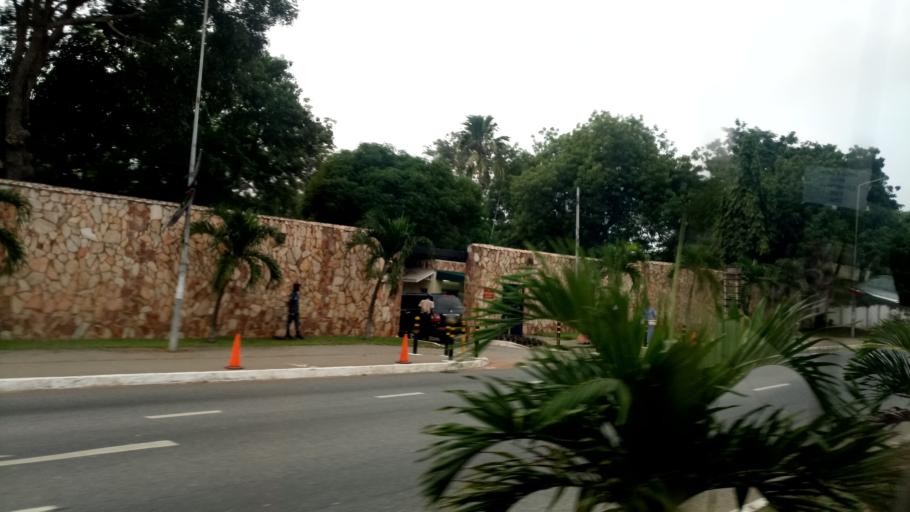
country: GH
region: Greater Accra
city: Accra
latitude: 5.5704
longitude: -0.1915
